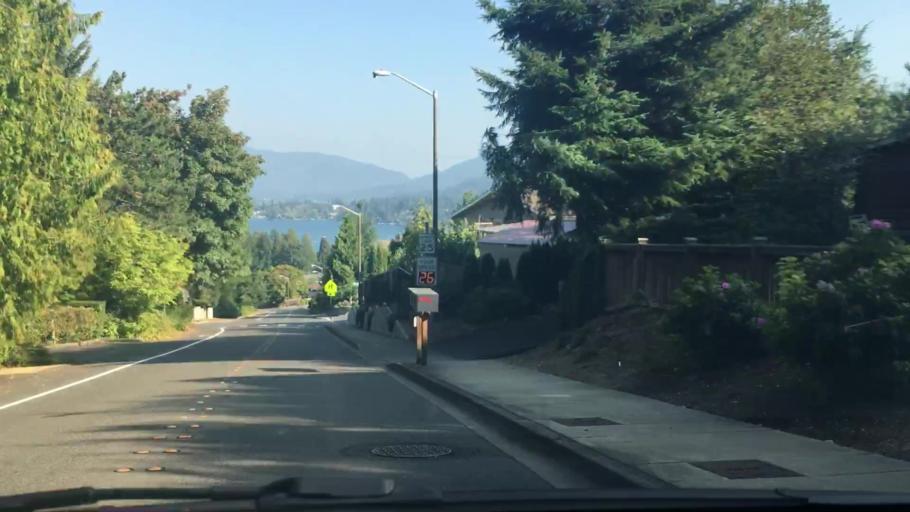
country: US
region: Washington
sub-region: King County
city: West Lake Sammamish
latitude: 47.5882
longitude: -122.1160
